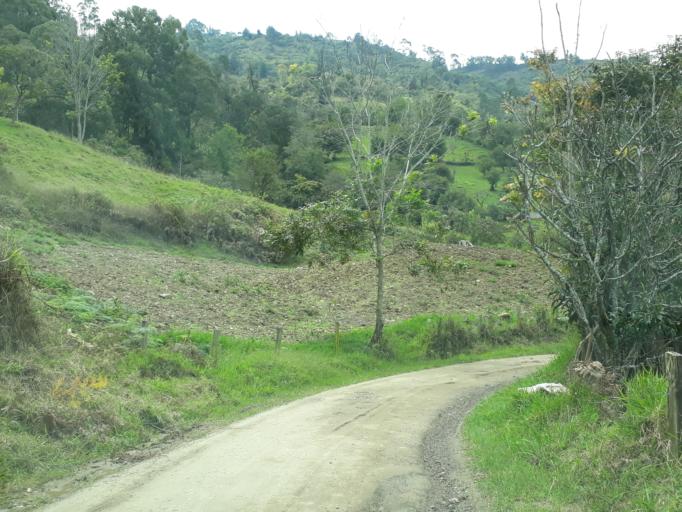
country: CO
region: Cundinamarca
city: Manta
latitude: 5.0136
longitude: -73.5429
